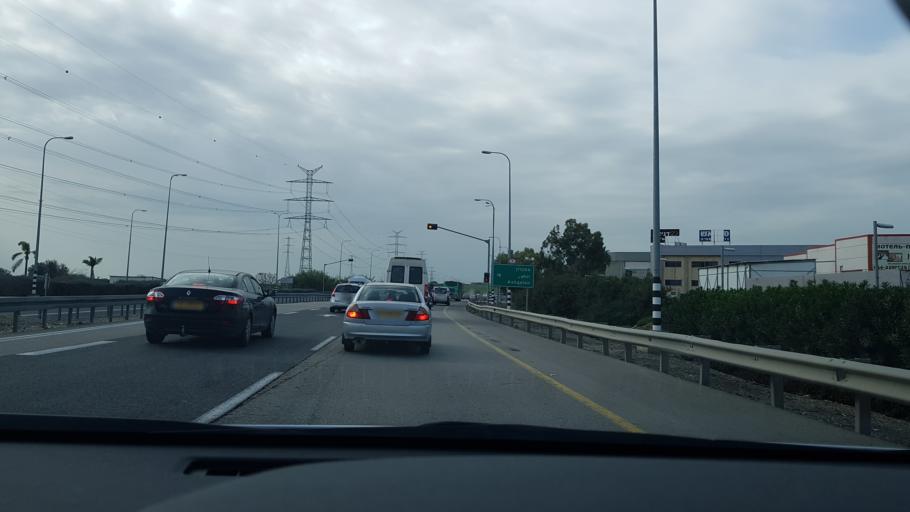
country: IL
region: Southern District
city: Ashdod
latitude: 31.7623
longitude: 34.6673
